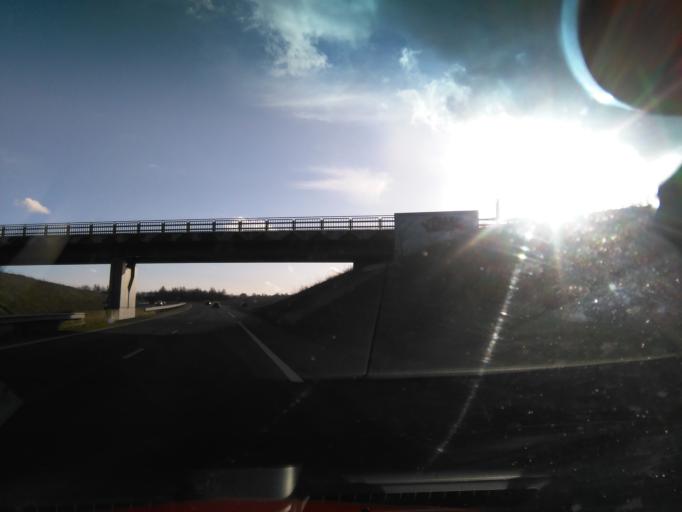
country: FR
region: Lower Normandy
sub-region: Departement du Calvados
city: Falaise
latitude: 48.9124
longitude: -0.2092
